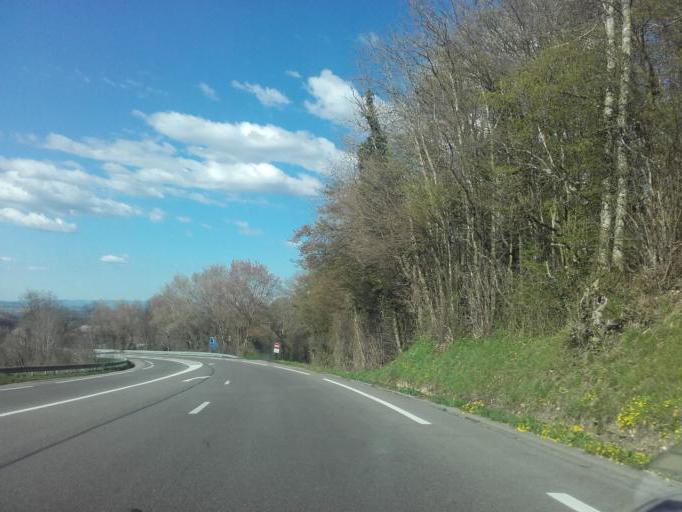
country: FR
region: Rhone-Alpes
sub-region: Departement de l'Isere
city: Nivolas-Vermelle
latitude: 45.5156
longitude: 5.3051
